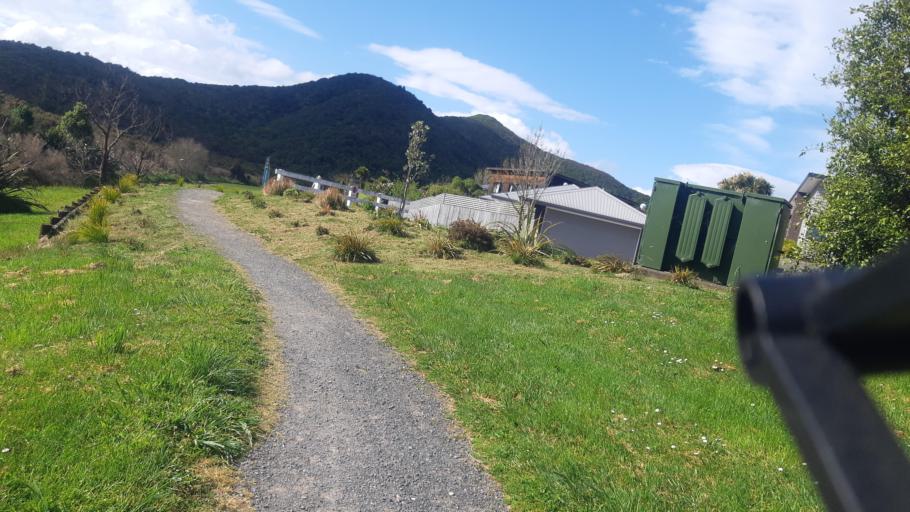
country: NZ
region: Marlborough
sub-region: Marlborough District
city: Picton
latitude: -41.2766
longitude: 174.0251
